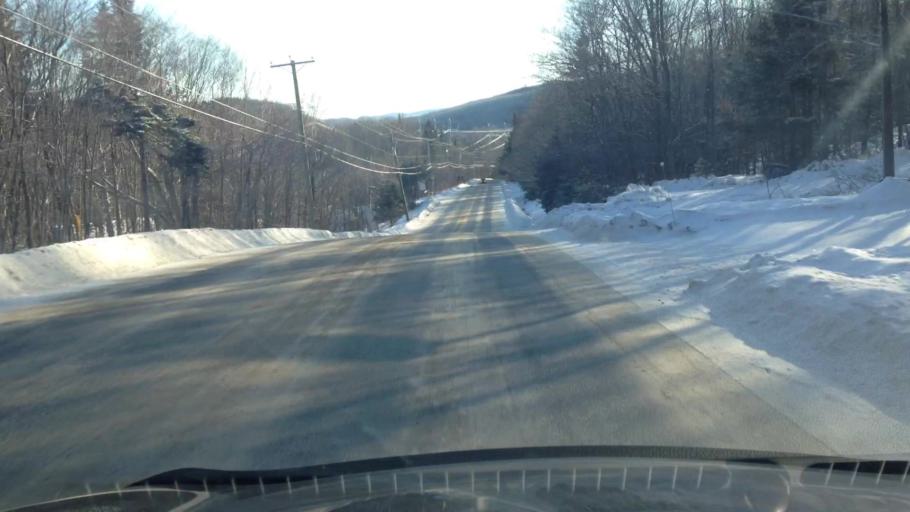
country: CA
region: Quebec
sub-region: Laurentides
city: Sainte-Agathe-des-Monts
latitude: 45.9360
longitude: -74.4405
